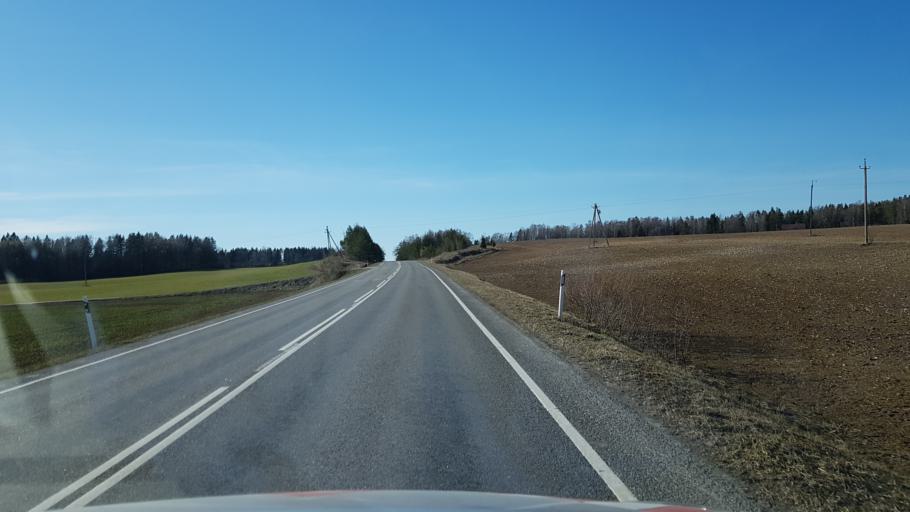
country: EE
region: Laeaene-Virumaa
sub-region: Vinni vald
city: Vinni
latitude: 59.3248
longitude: 26.4268
